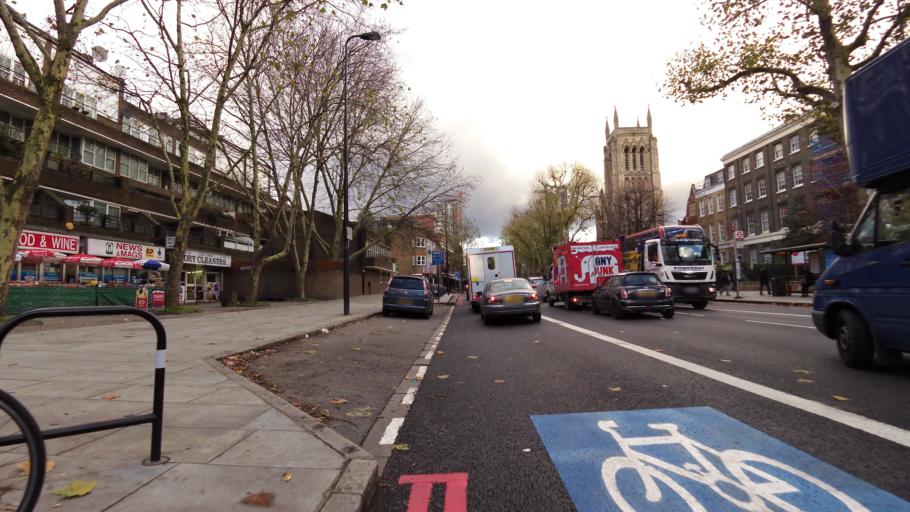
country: GB
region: England
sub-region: Greater London
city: Kennington
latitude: 51.4885
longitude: -0.1059
